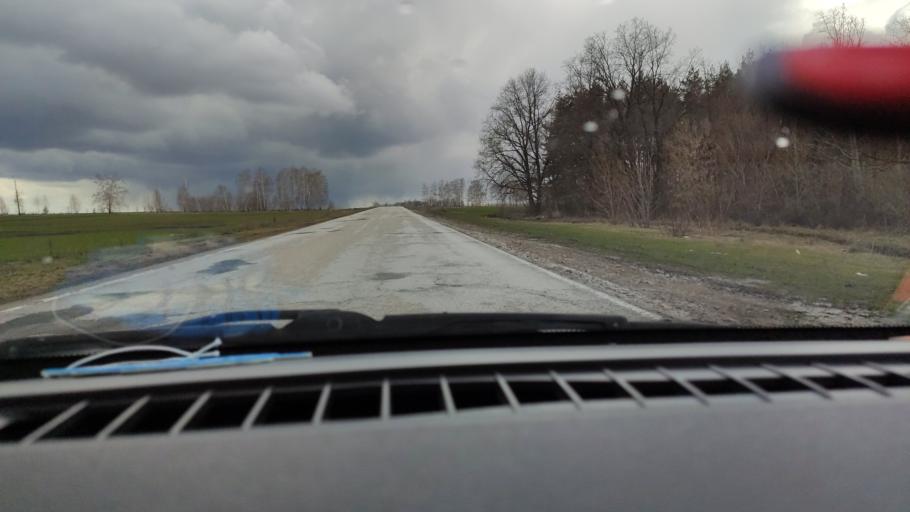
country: RU
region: Samara
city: Povolzhskiy
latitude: 53.8013
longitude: 49.7794
